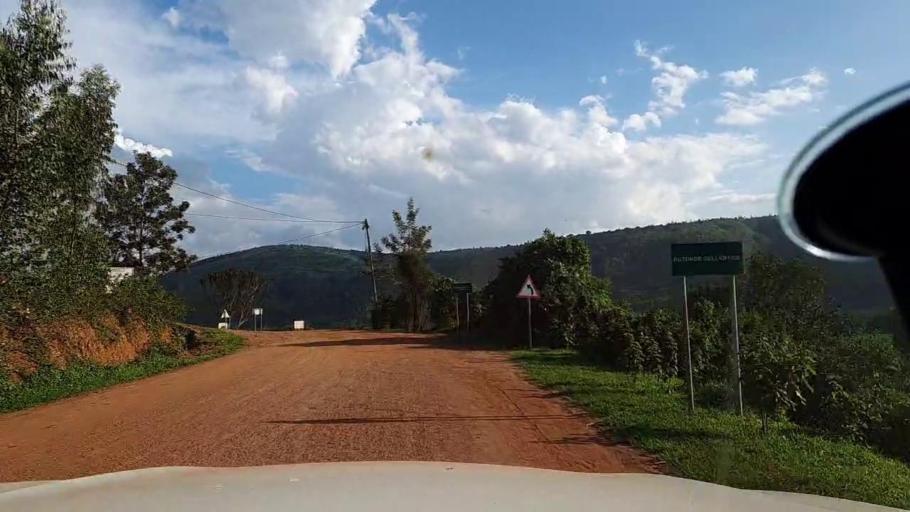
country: RW
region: Kigali
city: Kigali
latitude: -1.9021
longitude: 29.9642
